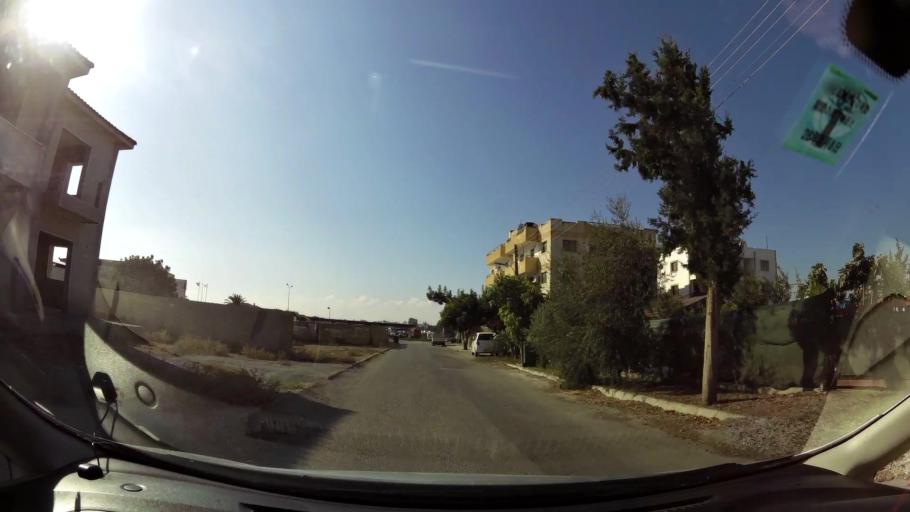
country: CY
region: Lefkosia
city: Nicosia
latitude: 35.2115
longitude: 33.3689
